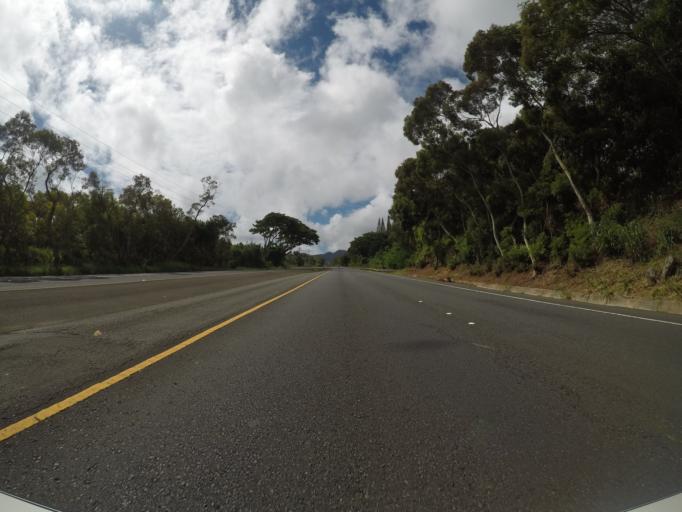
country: US
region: Hawaii
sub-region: Honolulu County
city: Waimanalo
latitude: 21.3643
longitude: -157.7377
